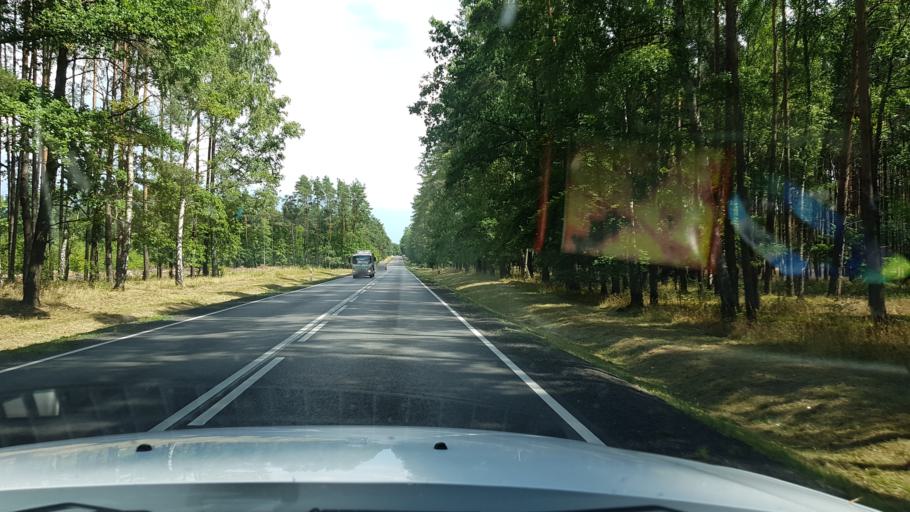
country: PL
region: West Pomeranian Voivodeship
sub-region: Powiat walecki
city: Walcz
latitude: 53.3102
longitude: 16.3789
